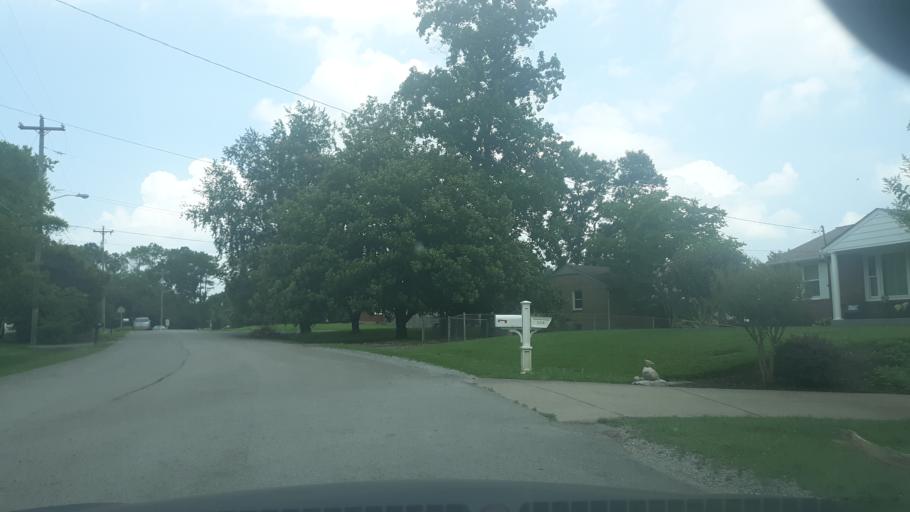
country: US
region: Tennessee
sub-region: Davidson County
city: Lakewood
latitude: 36.1836
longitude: -86.6496
